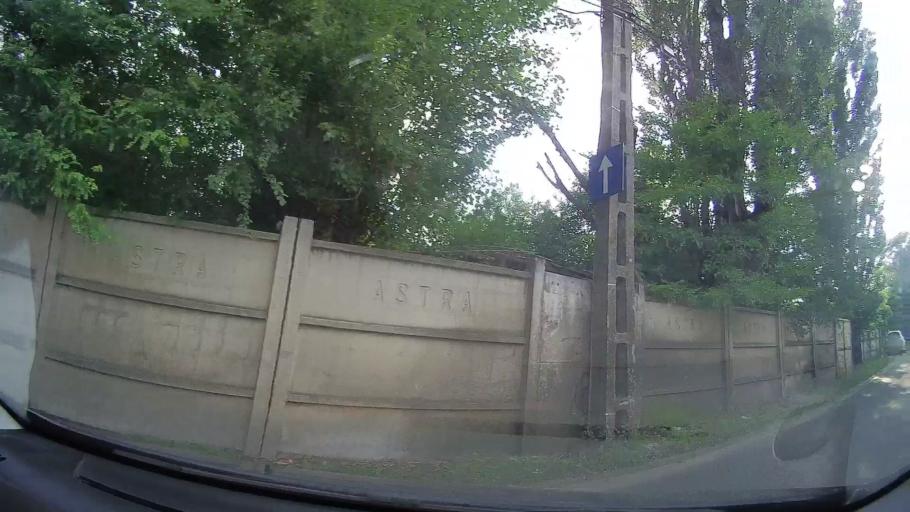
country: RO
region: Timis
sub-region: Comuna Dumbravita
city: Dumbravita
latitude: 45.7815
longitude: 21.2314
